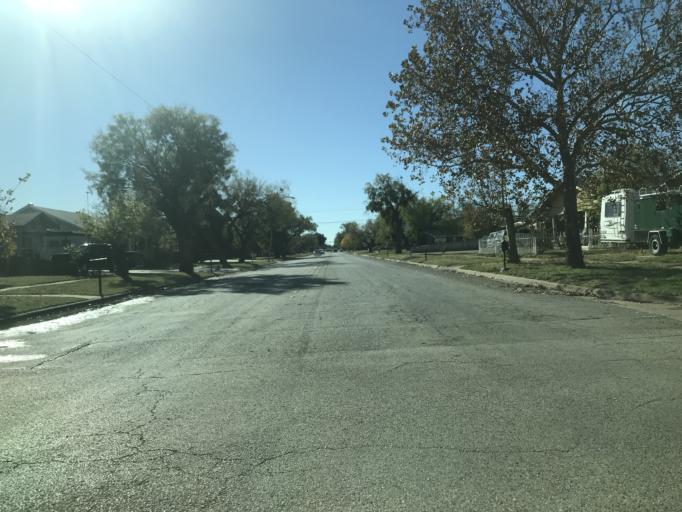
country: US
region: Texas
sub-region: Taylor County
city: Abilene
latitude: 32.4639
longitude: -99.7354
